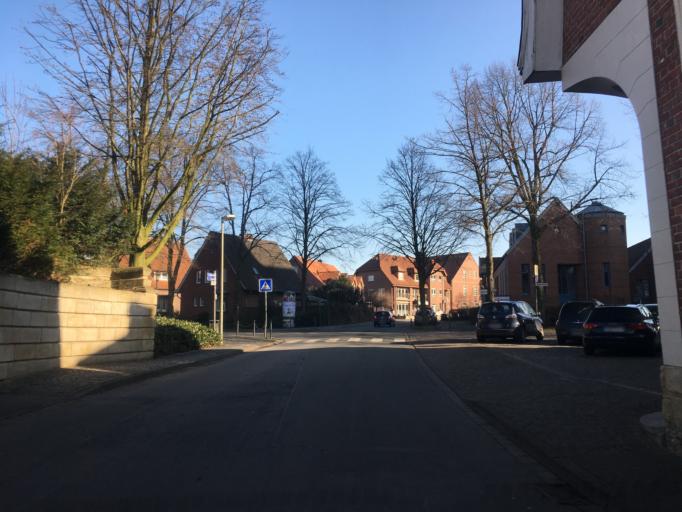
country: DE
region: North Rhine-Westphalia
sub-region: Regierungsbezirk Munster
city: Billerbeck
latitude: 51.9785
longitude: 7.2908
